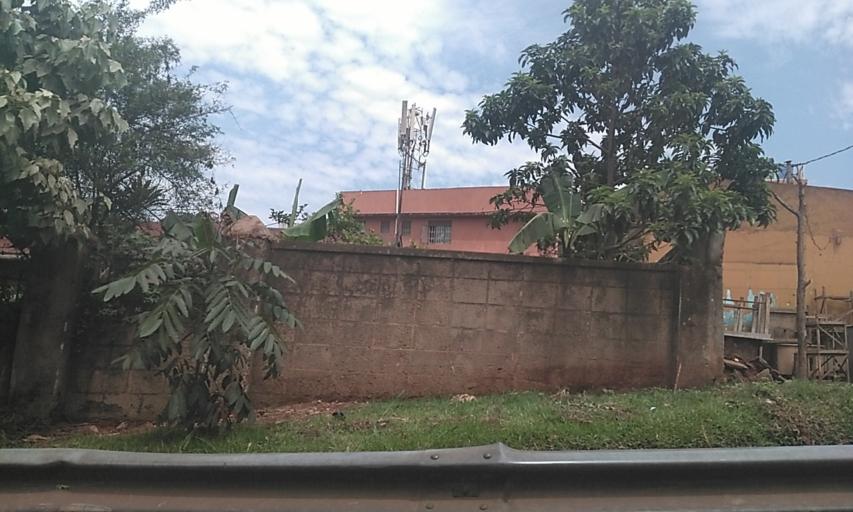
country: UG
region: Central Region
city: Kampala Central Division
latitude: 0.3044
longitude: 32.5460
